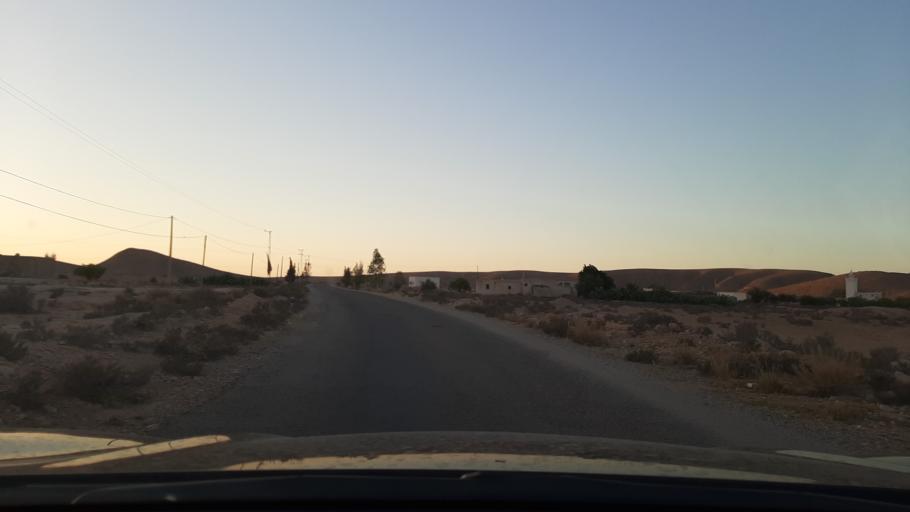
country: TN
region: Qabis
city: Matmata
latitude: 33.5671
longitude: 10.1780
